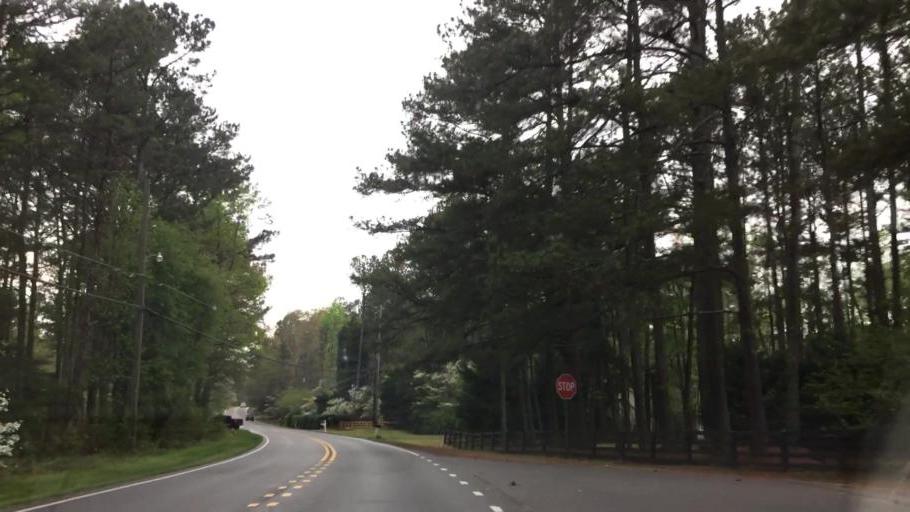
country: US
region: Georgia
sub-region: Fulton County
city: Milton
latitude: 34.1731
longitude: -84.2956
